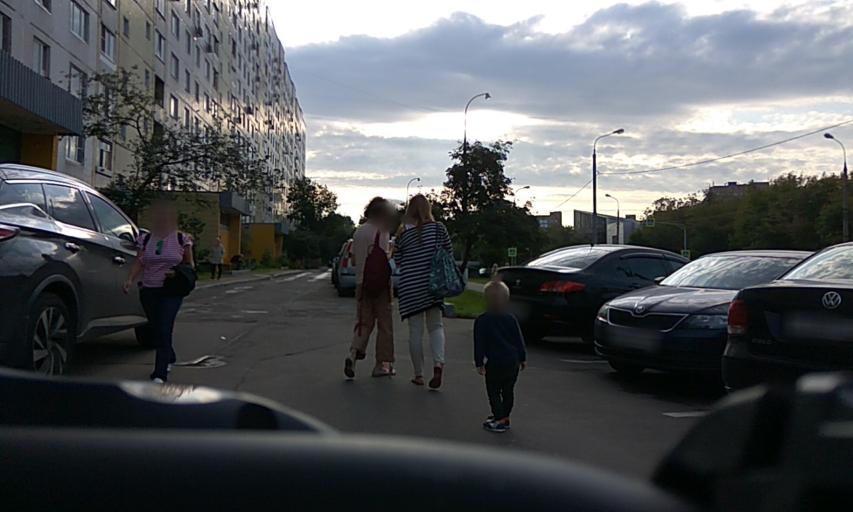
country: RU
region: Moscow
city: Kolomenskoye
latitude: 55.6783
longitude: 37.6955
